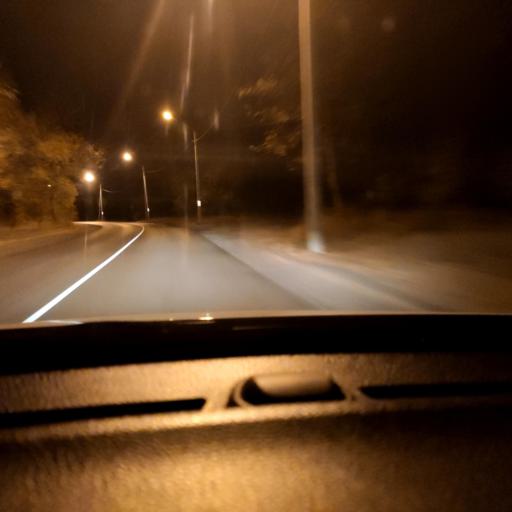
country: RU
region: Voronezj
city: Somovo
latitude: 51.7308
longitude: 39.3292
